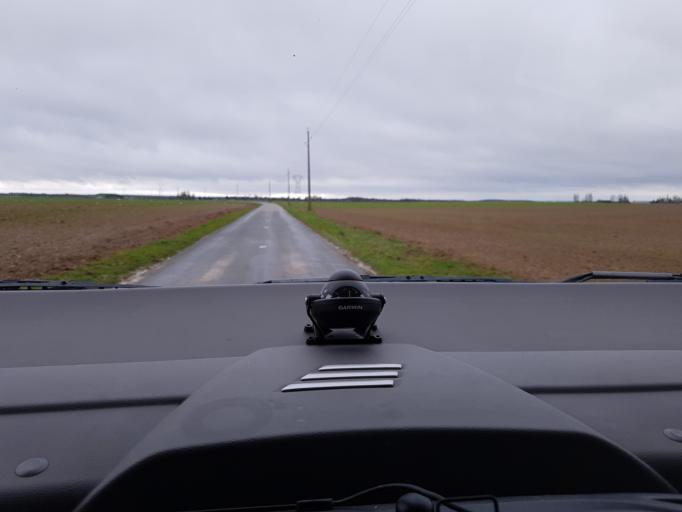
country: FR
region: Haute-Normandie
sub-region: Departement de l'Eure
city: Pont-Saint-Pierre
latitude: 49.2994
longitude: 1.3285
